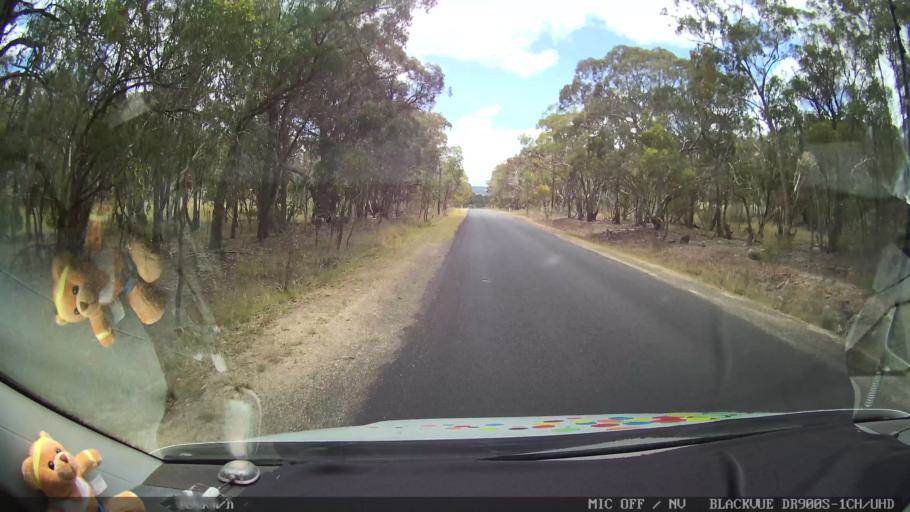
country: AU
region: New South Wales
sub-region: Glen Innes Severn
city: Glen Innes
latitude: -29.4296
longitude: 151.6423
